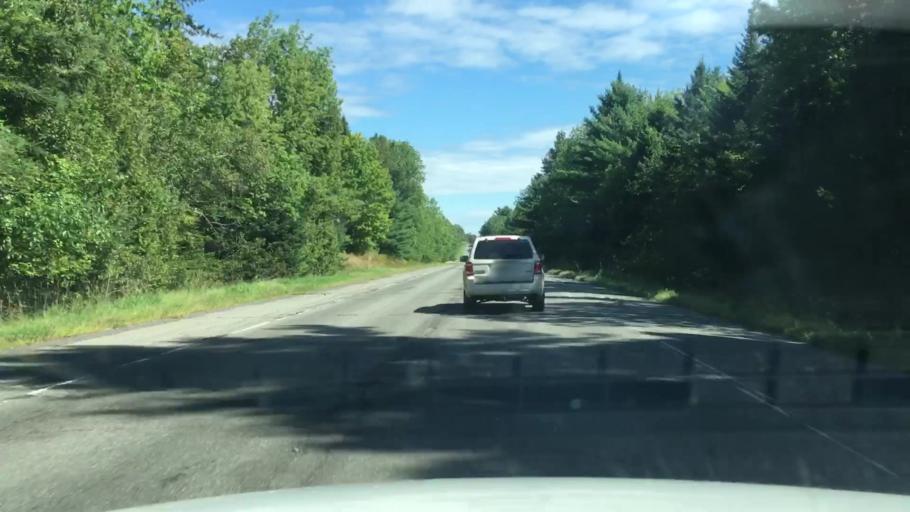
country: US
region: Maine
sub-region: Penobscot County
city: Dexter
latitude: 45.0536
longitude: -69.2585
